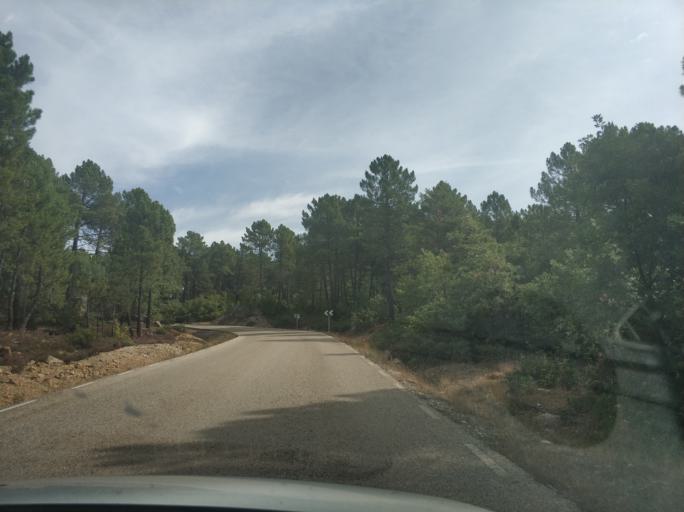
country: ES
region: Castille and Leon
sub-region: Provincia de Soria
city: Duruelo de la Sierra
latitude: 41.8953
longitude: -2.9445
